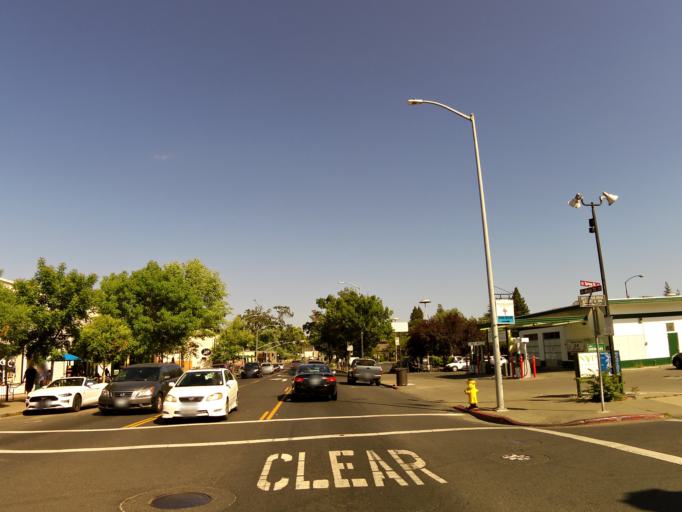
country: US
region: California
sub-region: Napa County
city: Saint Helena
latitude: 38.5039
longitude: -122.4681
